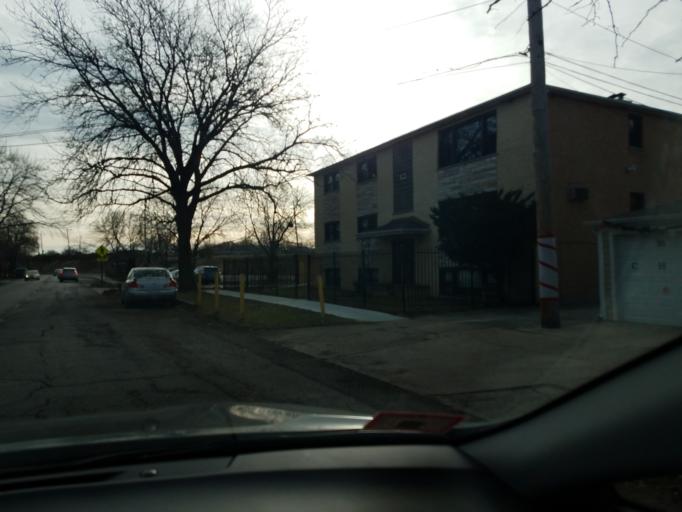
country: US
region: Illinois
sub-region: Cook County
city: Lincolnwood
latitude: 41.9796
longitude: -87.7554
